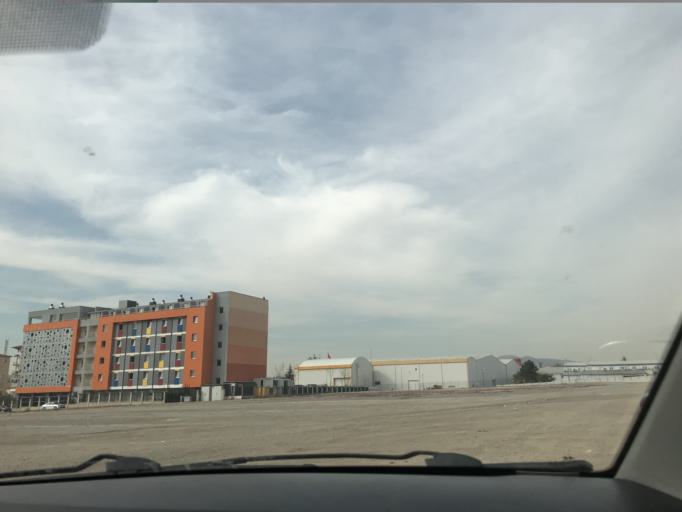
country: TR
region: Ankara
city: Batikent
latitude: 39.9632
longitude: 32.7675
